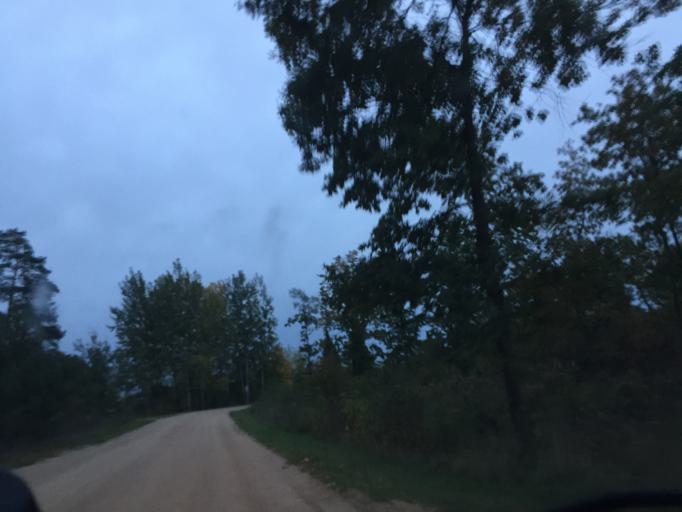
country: LV
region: Adazi
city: Adazi
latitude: 57.0832
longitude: 24.3649
